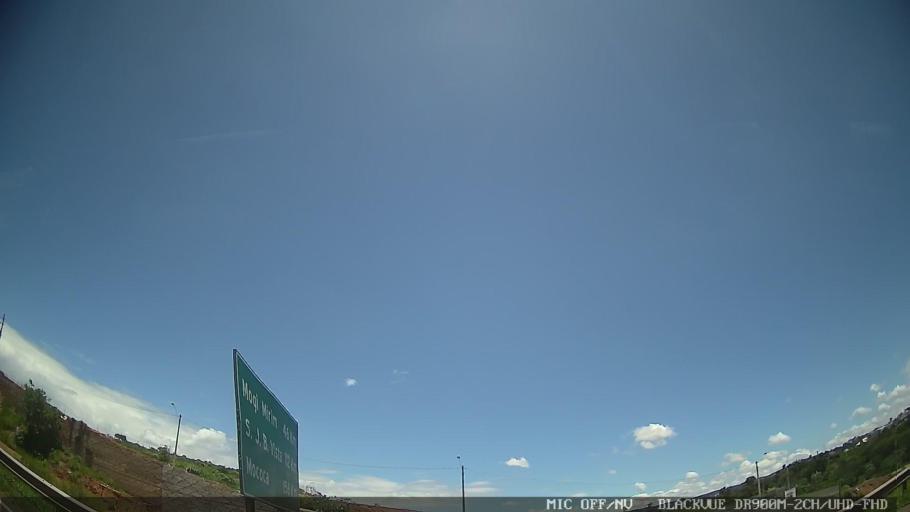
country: BR
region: Sao Paulo
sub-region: Campinas
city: Campinas
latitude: -22.8340
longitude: -47.0331
